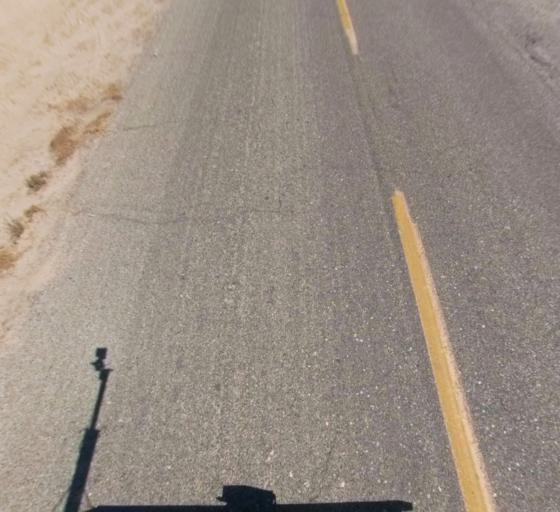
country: US
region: California
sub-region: Fresno County
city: Biola
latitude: 36.8647
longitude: -120.0194
